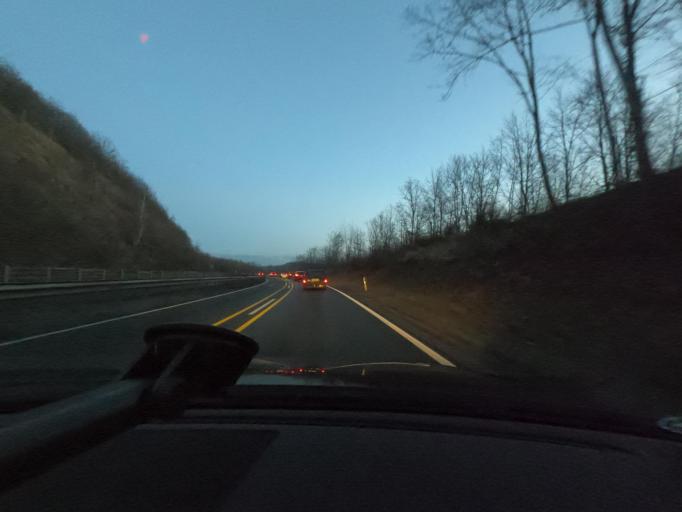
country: DE
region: Lower Saxony
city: Herzberg am Harz
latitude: 51.6253
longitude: 10.4014
